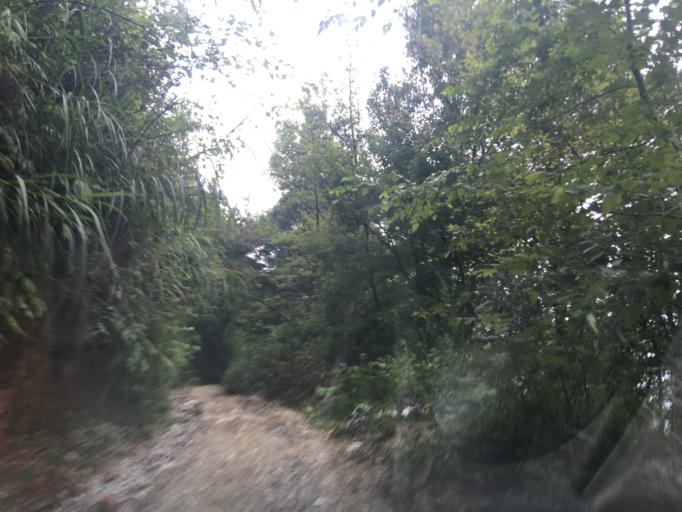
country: CN
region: Guangxi Zhuangzu Zizhiqu
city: Xinzhou
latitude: 25.1622
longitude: 105.6890
